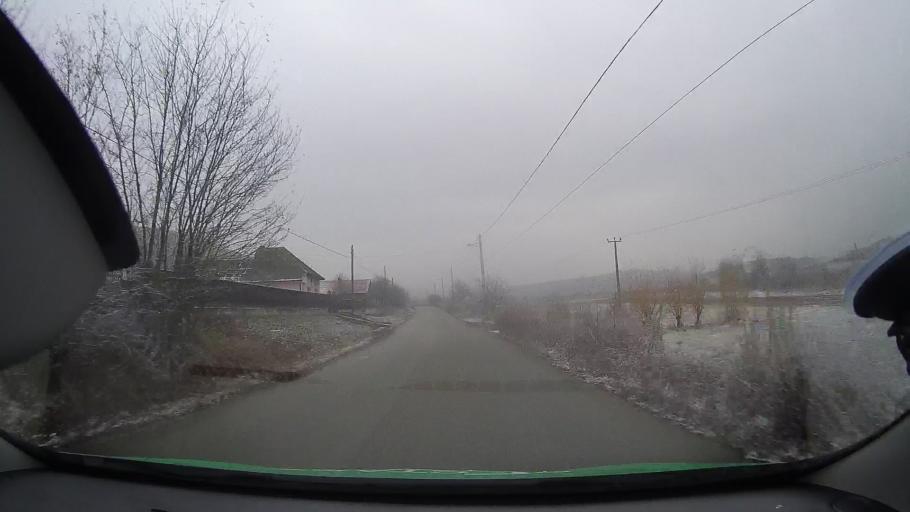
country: RO
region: Alba
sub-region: Comuna Noslac
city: Noslac
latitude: 46.3407
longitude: 23.9475
